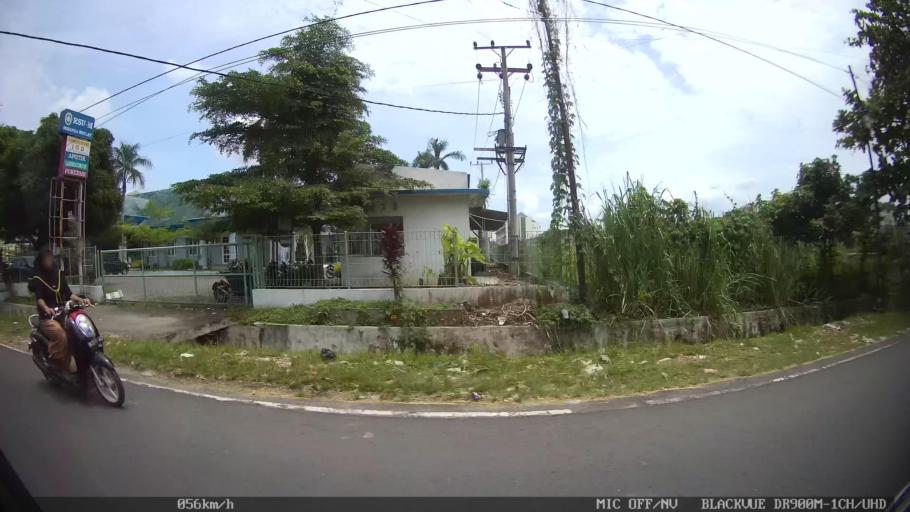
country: ID
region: North Sumatra
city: Sunggal
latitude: 3.5551
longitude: 98.6402
